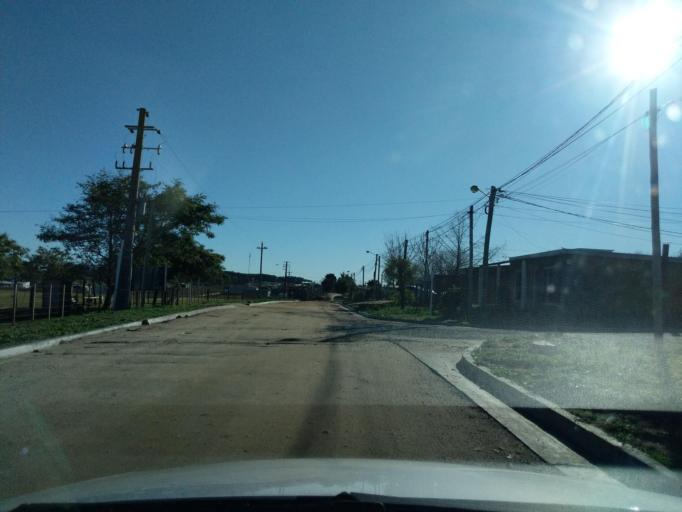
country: UY
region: Florida
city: Florida
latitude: -34.0860
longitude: -56.2403
